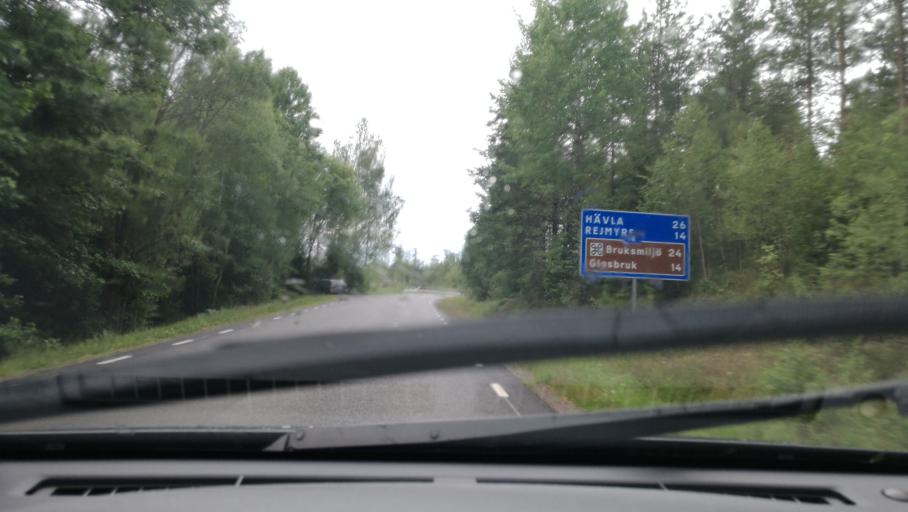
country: SE
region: OEstergoetland
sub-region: Norrkopings Kommun
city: Jursla
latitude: 58.7971
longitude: 16.1523
